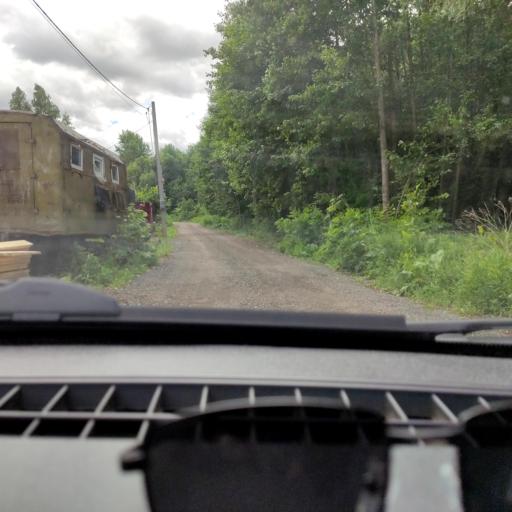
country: RU
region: Bashkortostan
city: Kabakovo
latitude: 54.6701
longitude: 56.0978
